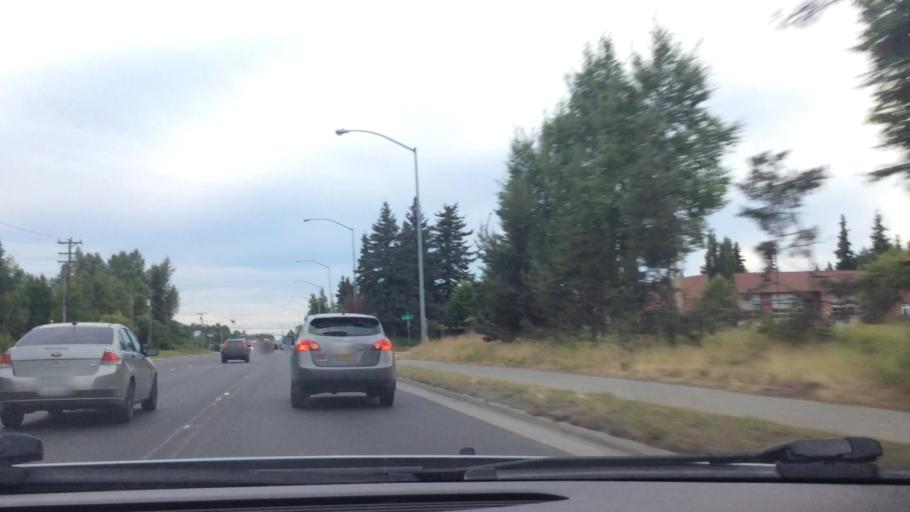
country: US
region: Alaska
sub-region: Anchorage Municipality
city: Anchorage
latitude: 61.1809
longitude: -149.8482
